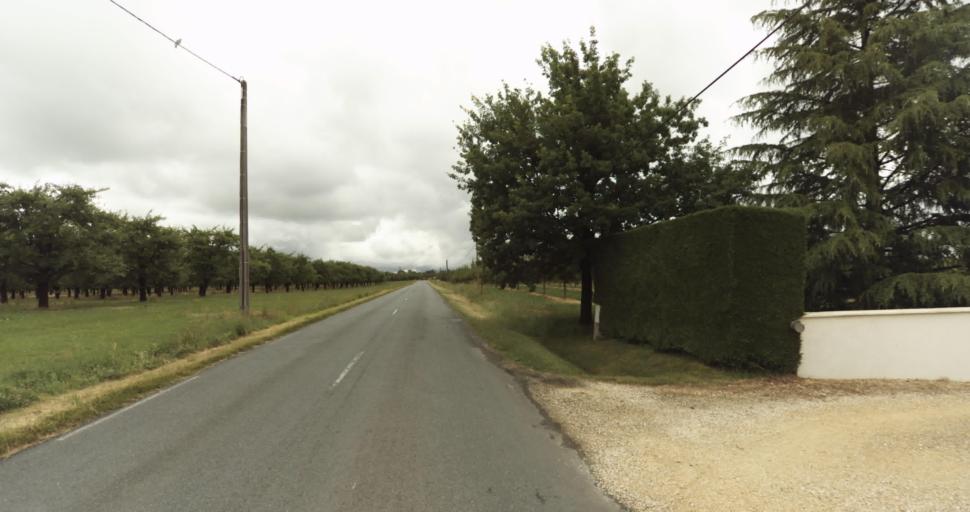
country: FR
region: Aquitaine
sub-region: Departement de la Dordogne
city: Beaumont-du-Perigord
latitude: 44.7346
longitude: 0.7852
